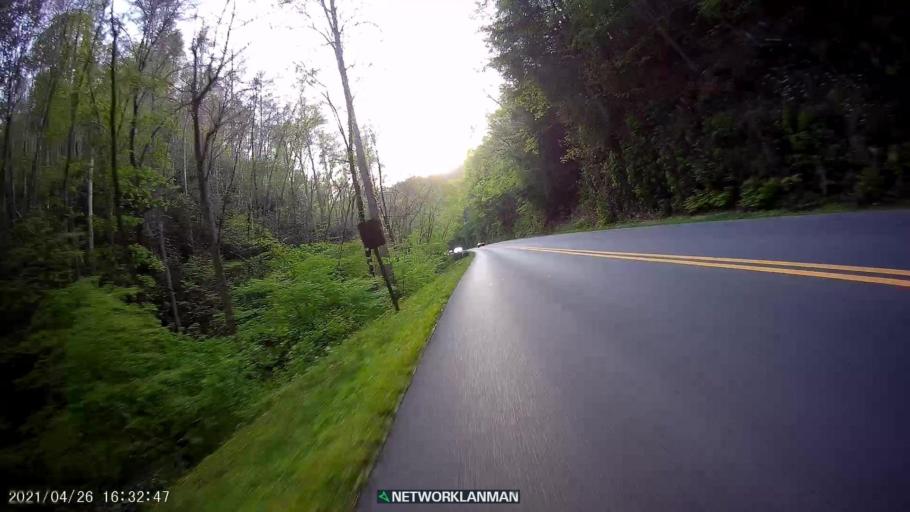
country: US
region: Tennessee
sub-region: Sevier County
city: Gatlinburg
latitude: 35.6386
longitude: -83.7177
